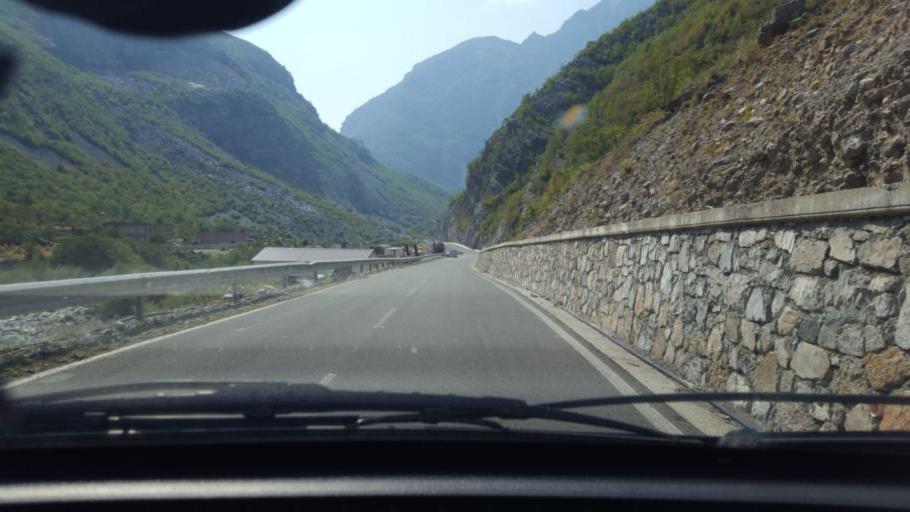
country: AL
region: Shkoder
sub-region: Rrethi i Malesia e Madhe
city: Kastrat
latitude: 42.5039
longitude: 19.5958
